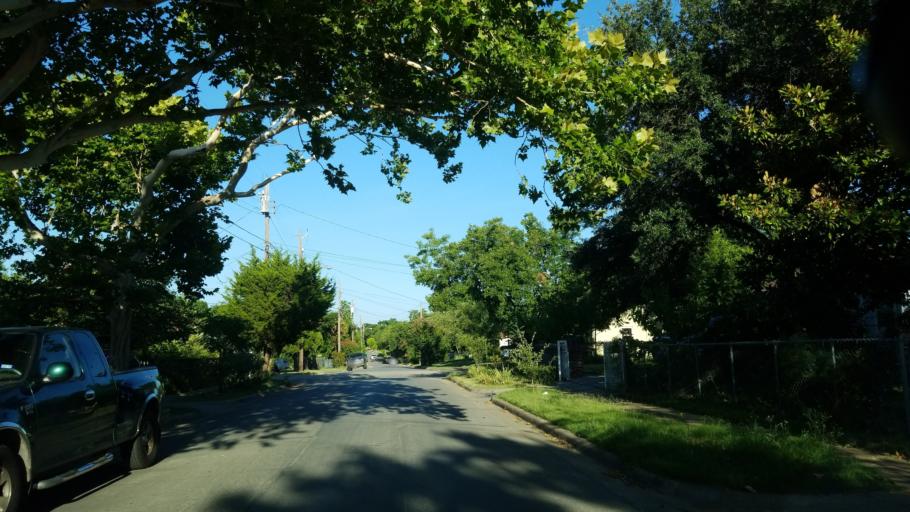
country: US
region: Texas
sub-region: Dallas County
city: Balch Springs
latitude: 32.7773
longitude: -96.7078
